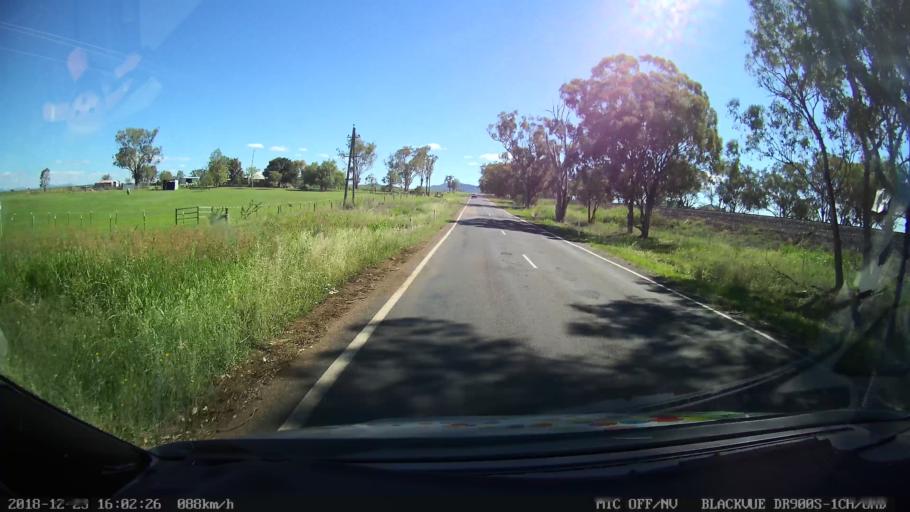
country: AU
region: New South Wales
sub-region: Tamworth Municipality
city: Phillip
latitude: -31.2323
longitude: 150.8090
